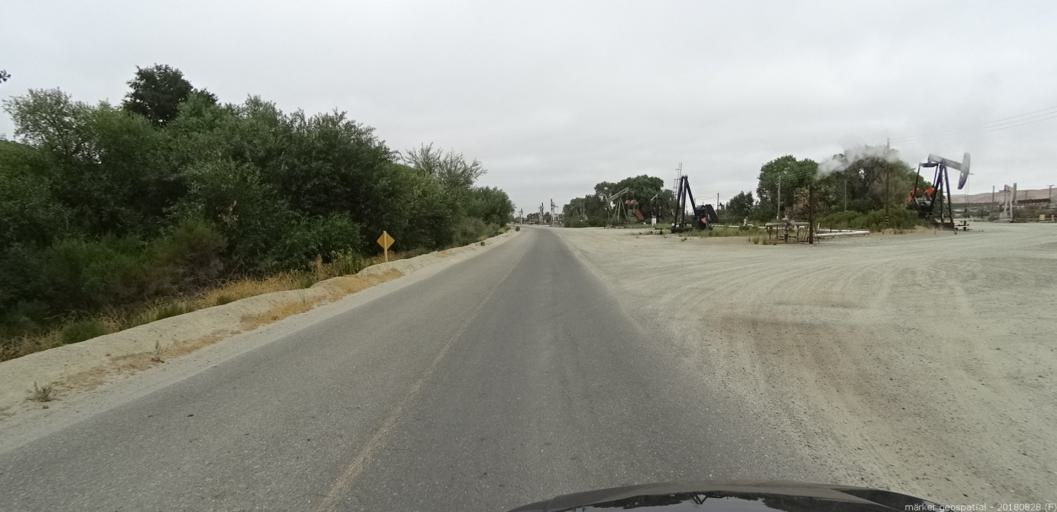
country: US
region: California
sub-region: San Luis Obispo County
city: Lake Nacimiento
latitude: 35.9562
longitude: -120.8760
